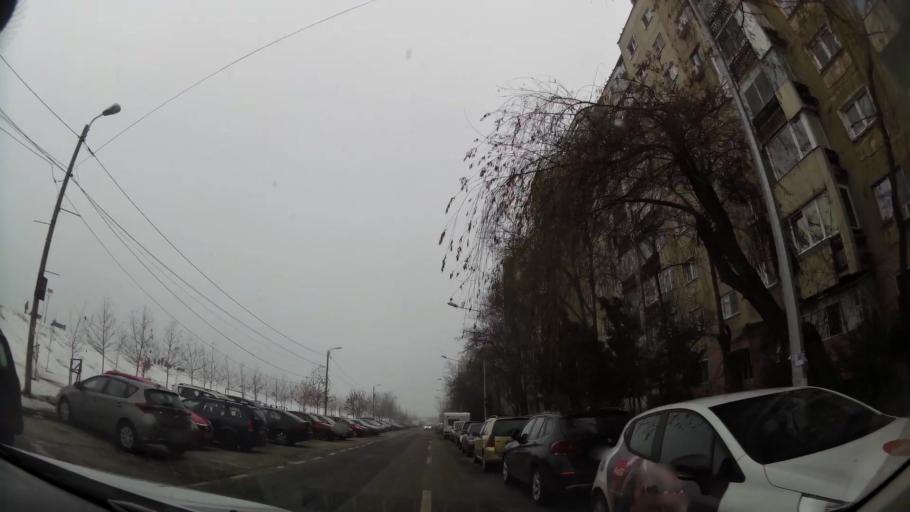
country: RO
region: Ilfov
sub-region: Comuna Chiajna
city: Rosu
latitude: 44.4528
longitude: 26.0401
